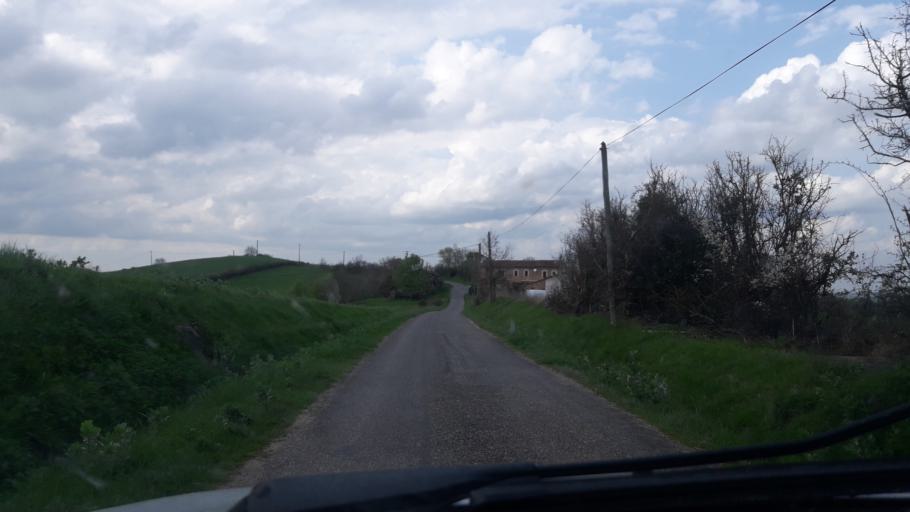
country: FR
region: Midi-Pyrenees
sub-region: Departement de l'Ariege
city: Lezat-sur-Leze
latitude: 43.1920
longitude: 1.3285
